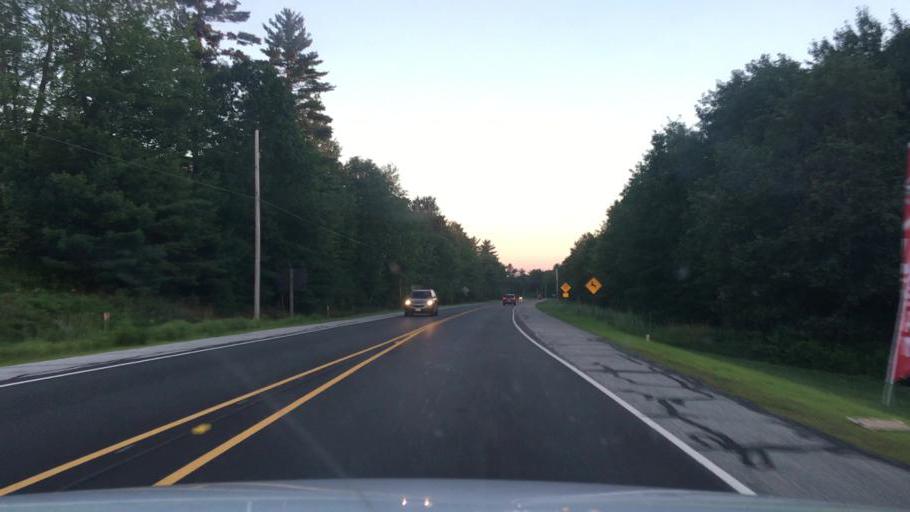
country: US
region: Maine
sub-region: Androscoggin County
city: Turner
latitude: 44.2494
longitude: -70.2595
